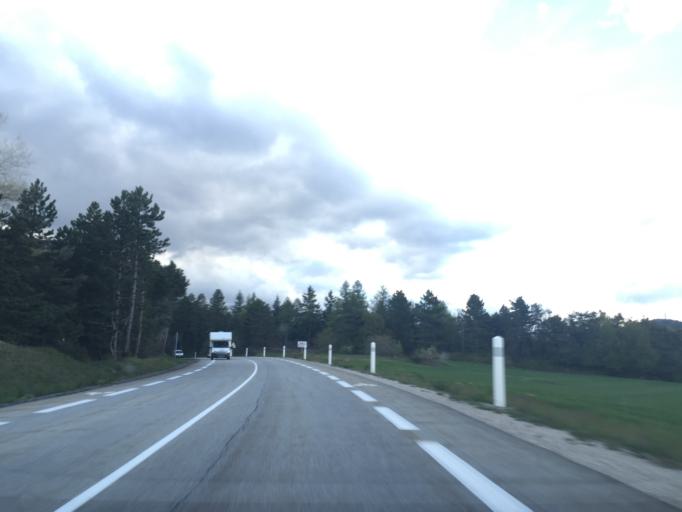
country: FR
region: Rhone-Alpes
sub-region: Departement de l'Isere
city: La Motte-Saint-Martin
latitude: 44.8764
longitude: 5.6255
